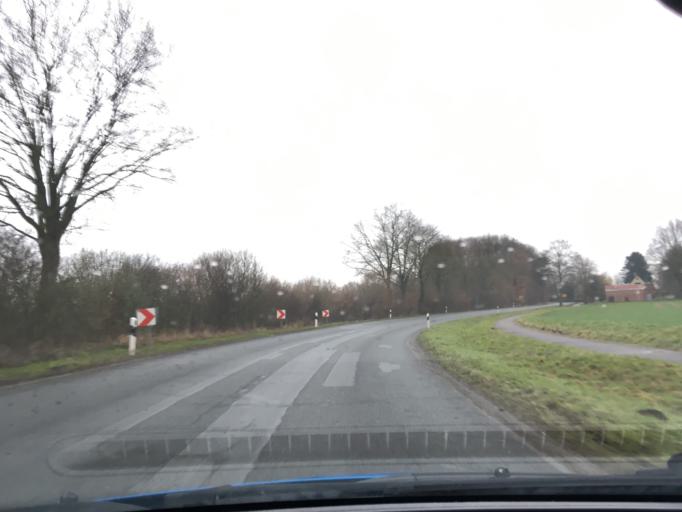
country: DE
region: Schleswig-Holstein
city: Breitenfelde
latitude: 53.5987
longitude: 10.6408
